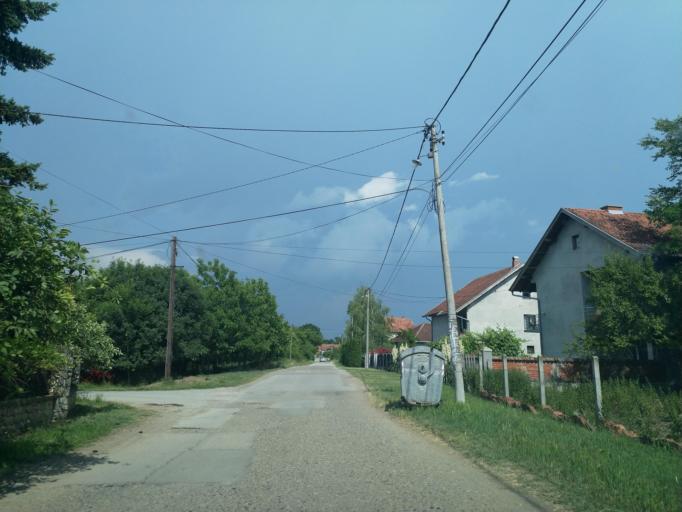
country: RS
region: Central Serbia
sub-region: Pomoravski Okrug
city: Cuprija
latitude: 43.9547
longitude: 21.3226
